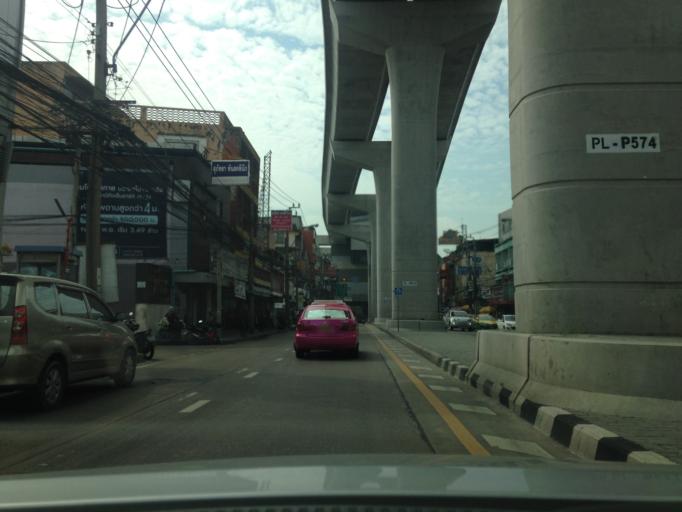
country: TH
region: Bangkok
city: Bang Sue
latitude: 13.8085
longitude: 100.5311
